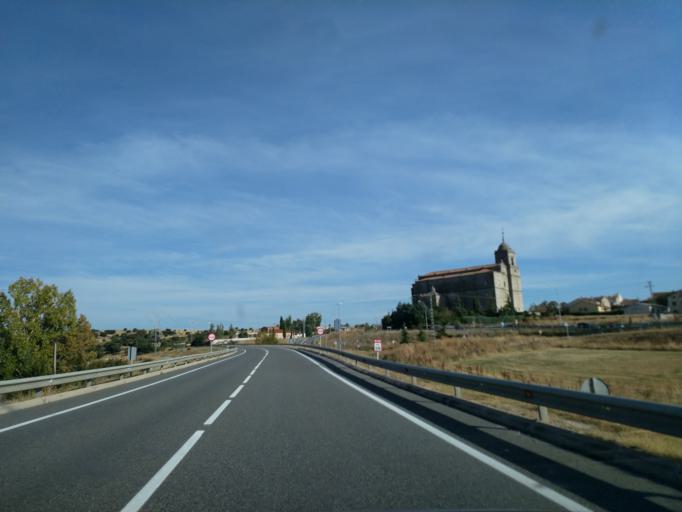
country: ES
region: Castille and Leon
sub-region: Provincia de Segovia
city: Villacastin
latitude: 40.7836
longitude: -4.4147
